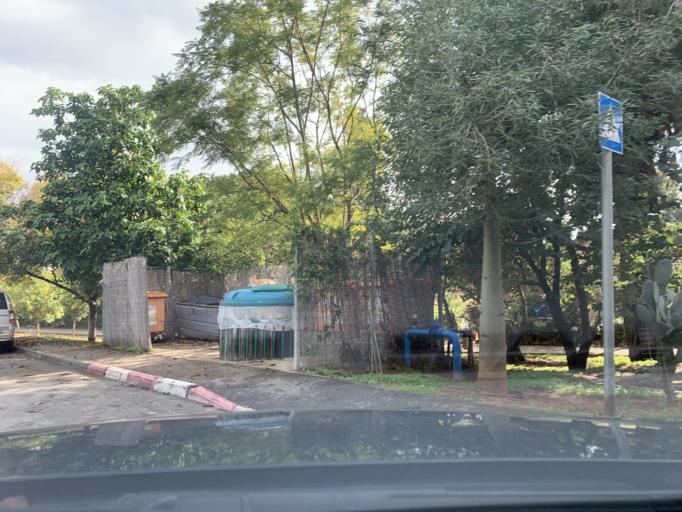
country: PS
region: West Bank
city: Qalqilyah
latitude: 32.1997
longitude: 34.9490
